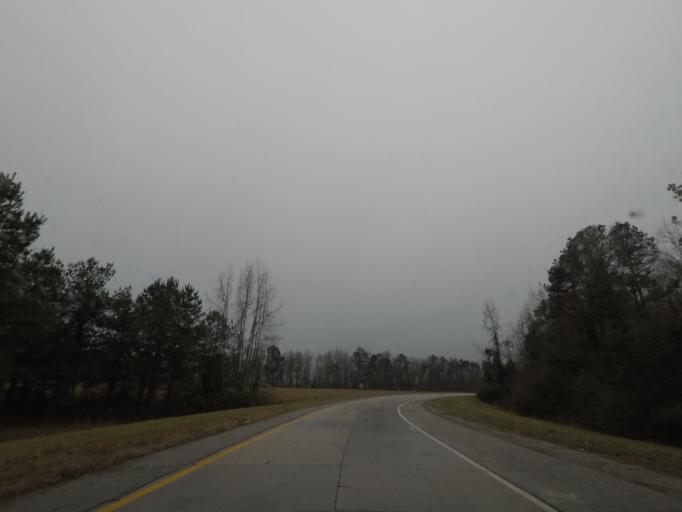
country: US
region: South Carolina
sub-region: Clarendon County
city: Manning
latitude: 33.7396
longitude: -80.2111
